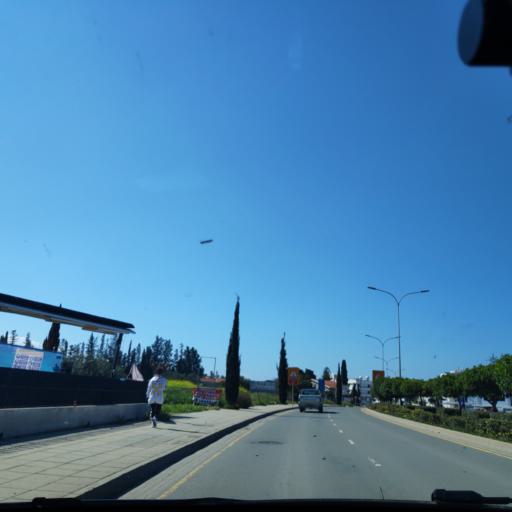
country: CY
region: Lefkosia
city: Tseri
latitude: 35.1109
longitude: 33.3084
